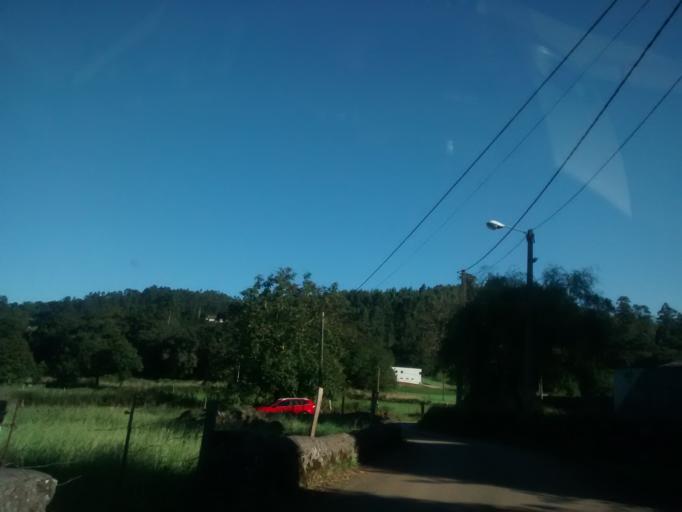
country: ES
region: Cantabria
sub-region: Provincia de Cantabria
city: Entrambasaguas
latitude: 43.3642
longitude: -3.6873
